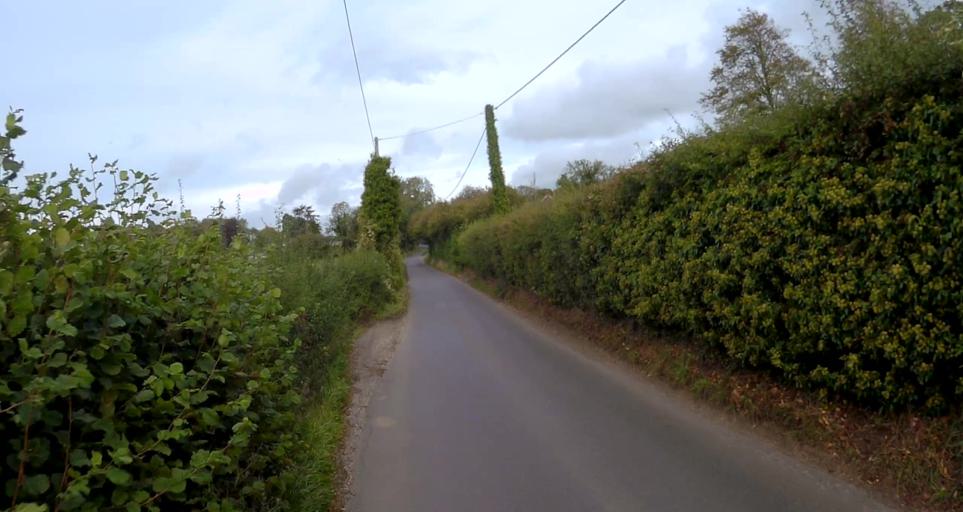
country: GB
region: England
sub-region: Hampshire
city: Four Marks
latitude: 51.1287
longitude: -1.0734
